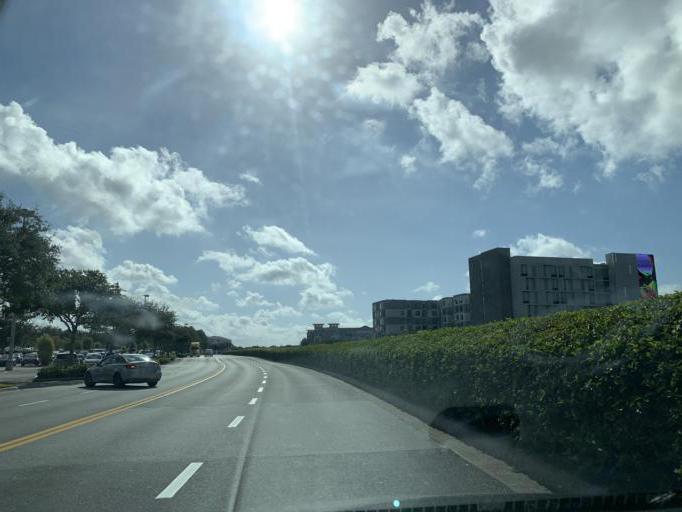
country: US
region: Florida
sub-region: Orange County
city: Oak Ridge
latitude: 28.4860
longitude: -81.4348
